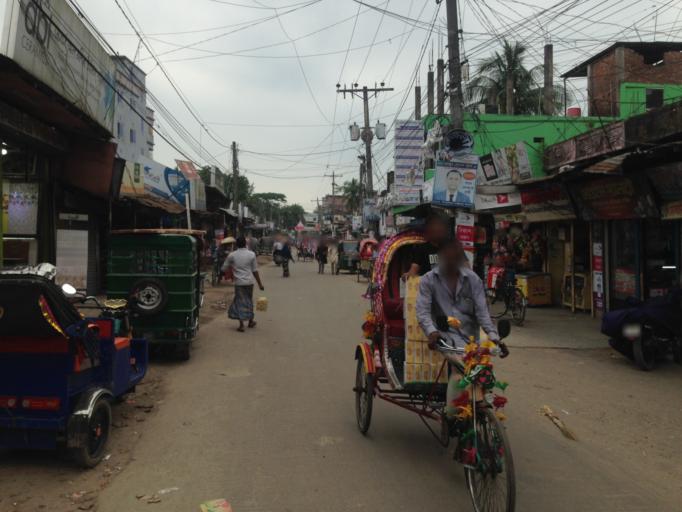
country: BD
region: Chittagong
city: Raipur
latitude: 23.0366
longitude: 90.7657
